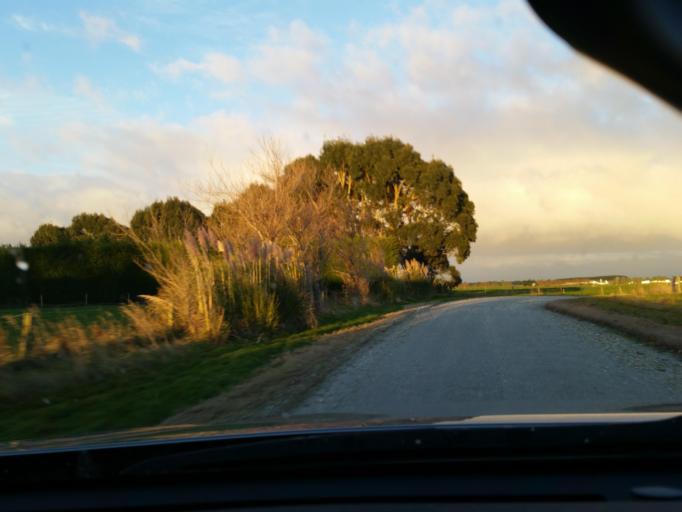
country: NZ
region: Southland
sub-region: Invercargill City
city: Invercargill
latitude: -46.4082
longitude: 168.7210
